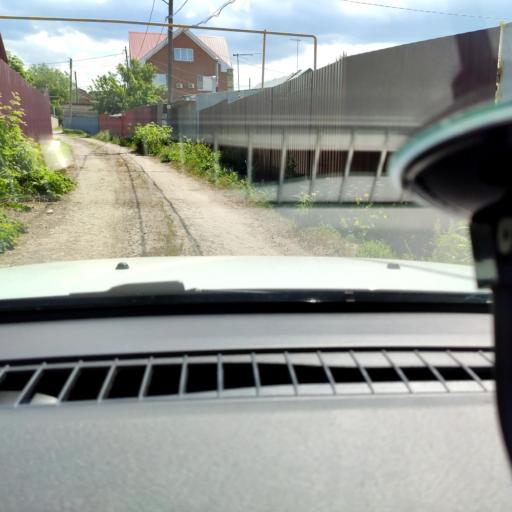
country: RU
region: Samara
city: Samara
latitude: 53.1749
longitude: 50.1630
